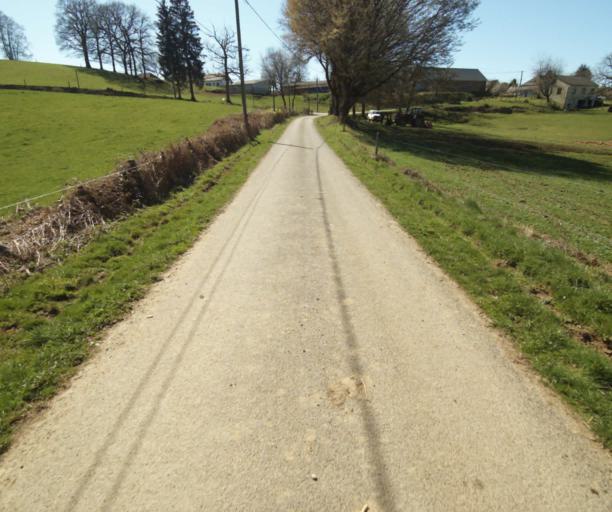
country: FR
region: Limousin
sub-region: Departement de la Correze
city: Seilhac
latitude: 45.3921
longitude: 1.6827
